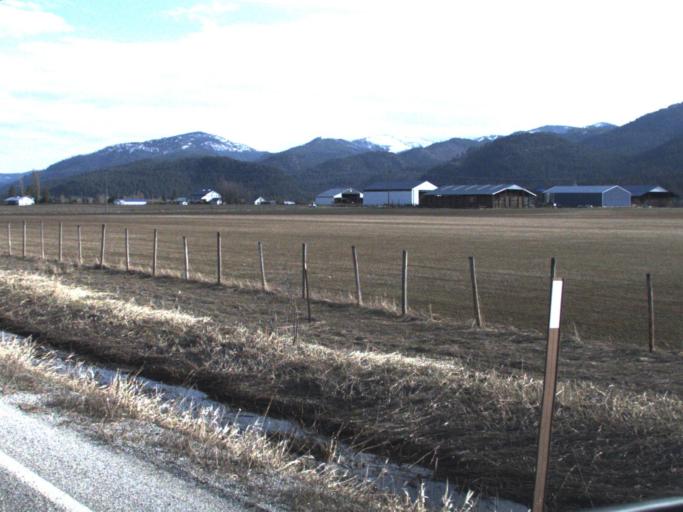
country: US
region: Washington
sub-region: Pend Oreille County
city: Newport
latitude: 48.3542
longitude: -117.3046
